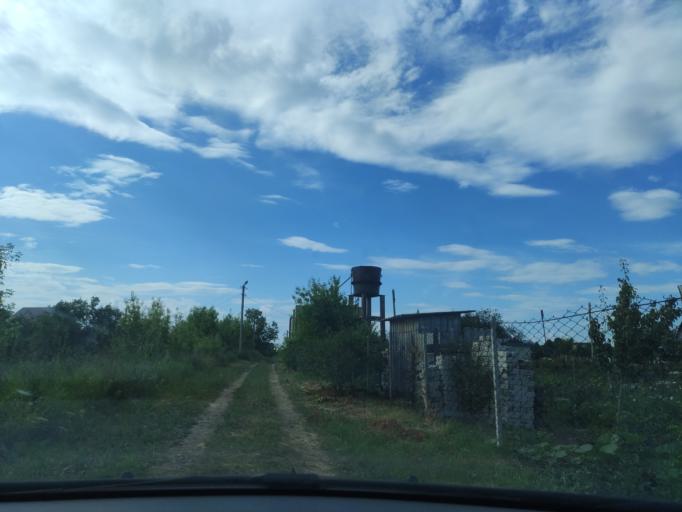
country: RU
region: Ulyanovsk
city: Cherdakly
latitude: 54.4428
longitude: 48.8960
